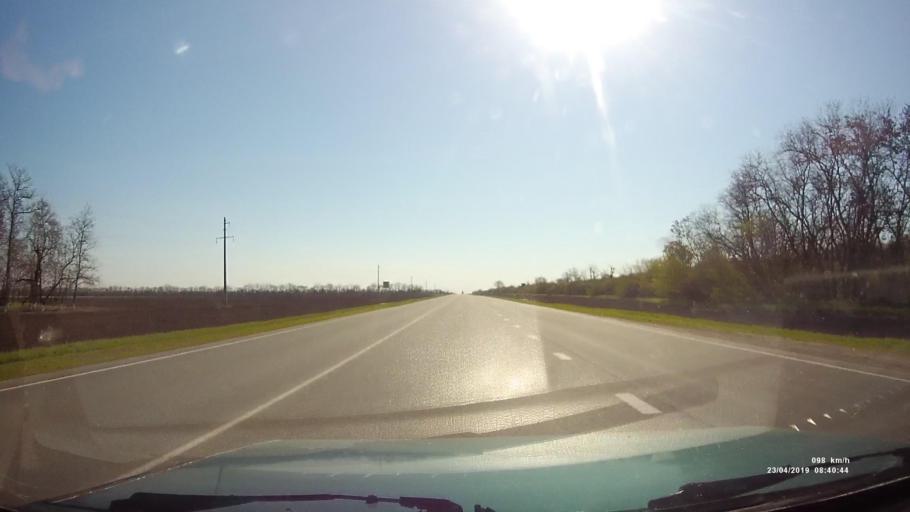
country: RU
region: Rostov
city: Gigant
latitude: 46.5255
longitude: 41.2352
